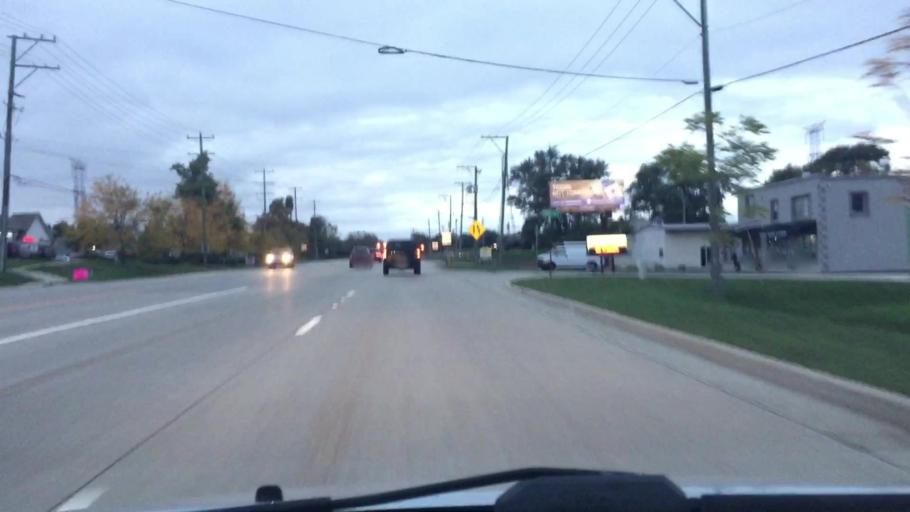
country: US
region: Illinois
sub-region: McHenry County
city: Crystal Lake
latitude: 42.2530
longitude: -88.2866
